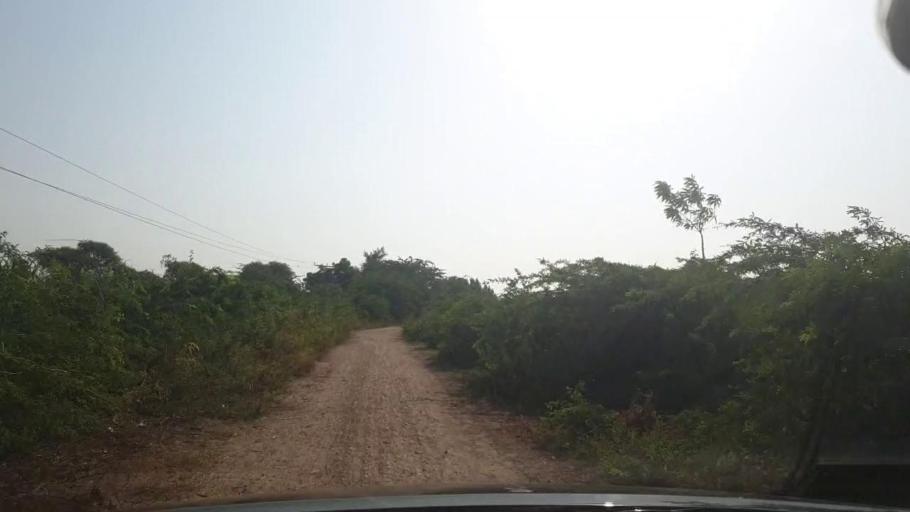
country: PK
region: Sindh
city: Tando Bago
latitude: 24.6509
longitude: 69.1732
